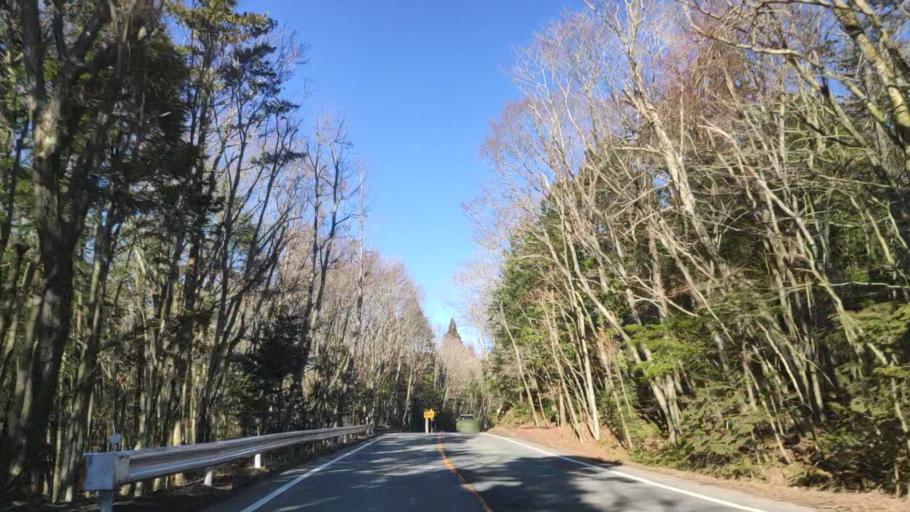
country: JP
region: Yamanashi
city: Fujikawaguchiko
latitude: 35.4503
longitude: 138.6429
